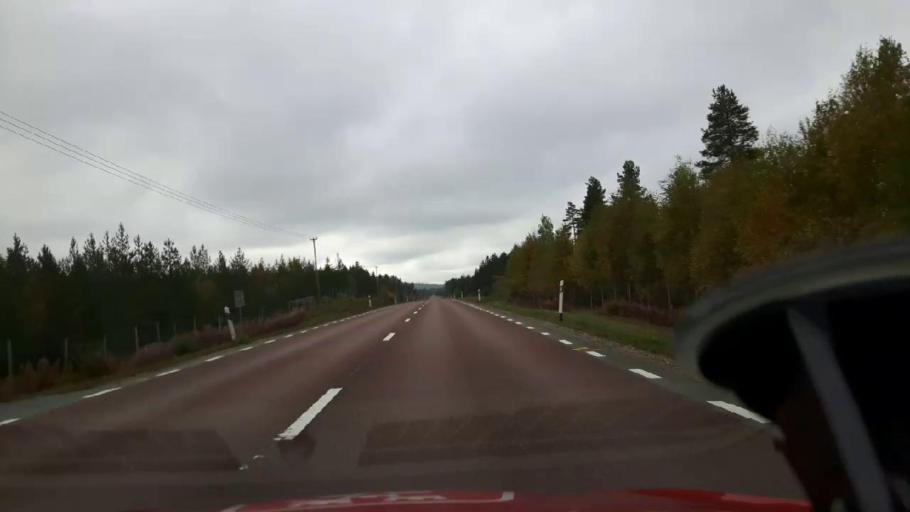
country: SE
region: Jaemtland
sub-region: Harjedalens Kommun
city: Sveg
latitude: 62.2395
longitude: 14.8316
